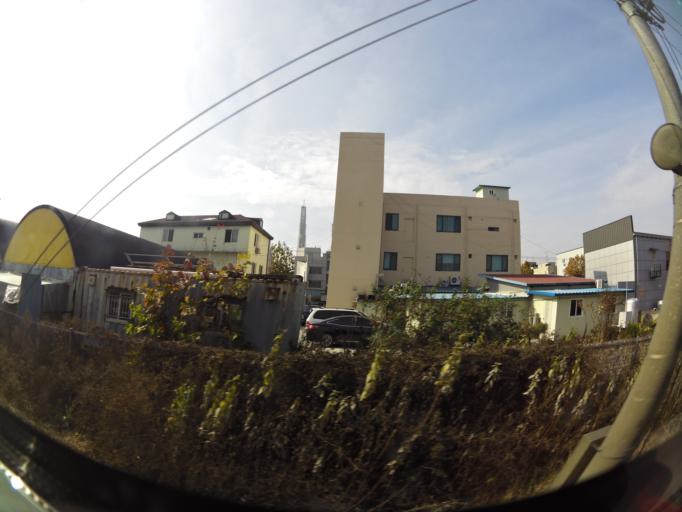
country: KR
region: Daejeon
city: Songgang-dong
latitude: 36.6071
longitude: 127.2944
